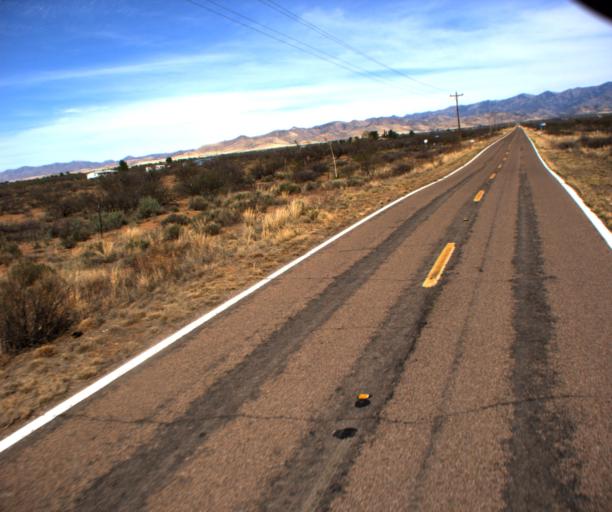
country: US
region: Arizona
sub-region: Cochise County
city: Willcox
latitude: 31.8760
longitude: -109.5544
